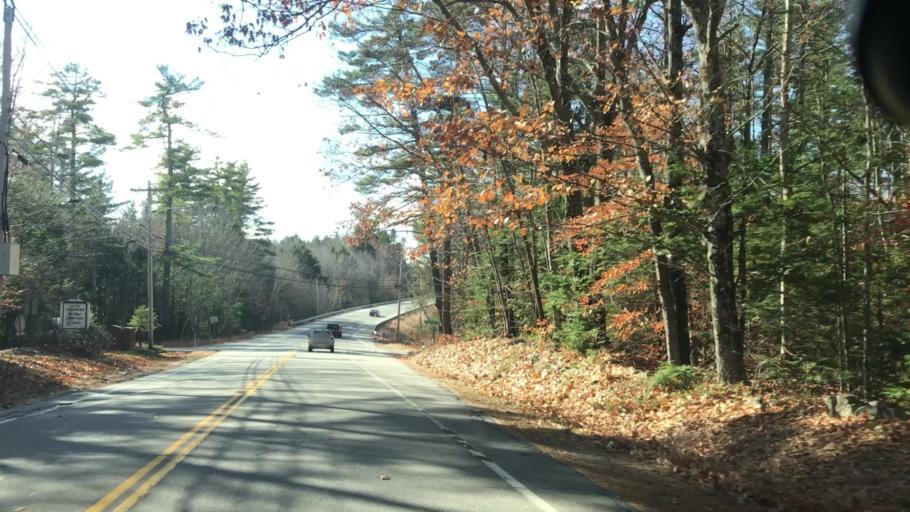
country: US
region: New Hampshire
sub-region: Carroll County
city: Wolfeboro
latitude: 43.5538
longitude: -71.1856
